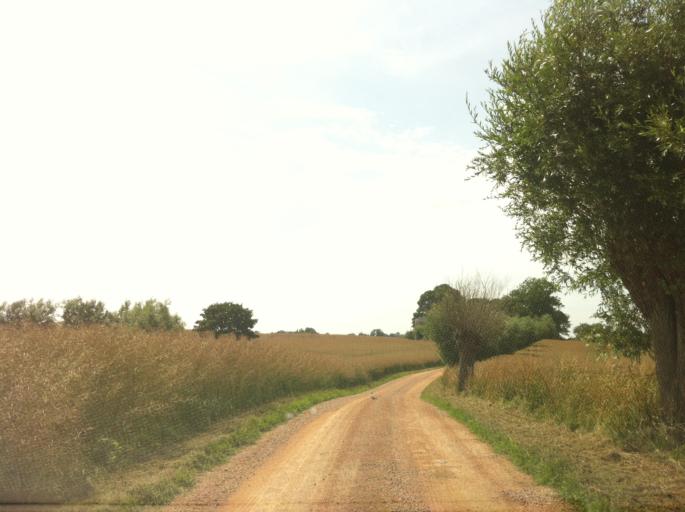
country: SE
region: Skane
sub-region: Skurups Kommun
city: Skurup
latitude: 55.4472
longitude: 13.4358
